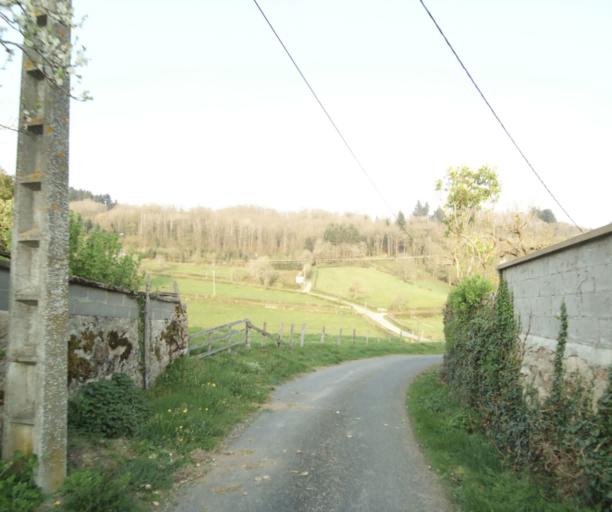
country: FR
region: Bourgogne
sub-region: Departement de Saone-et-Loire
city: Matour
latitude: 46.4319
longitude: 4.4613
